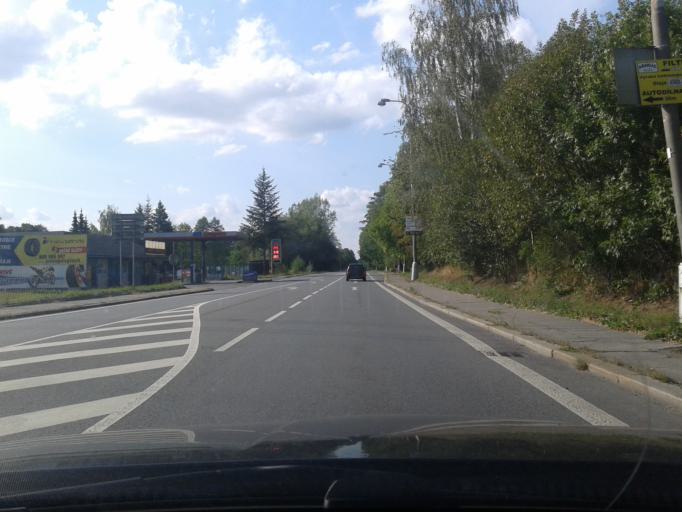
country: CZ
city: Dolni Lutyne
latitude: 49.8956
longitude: 18.4422
